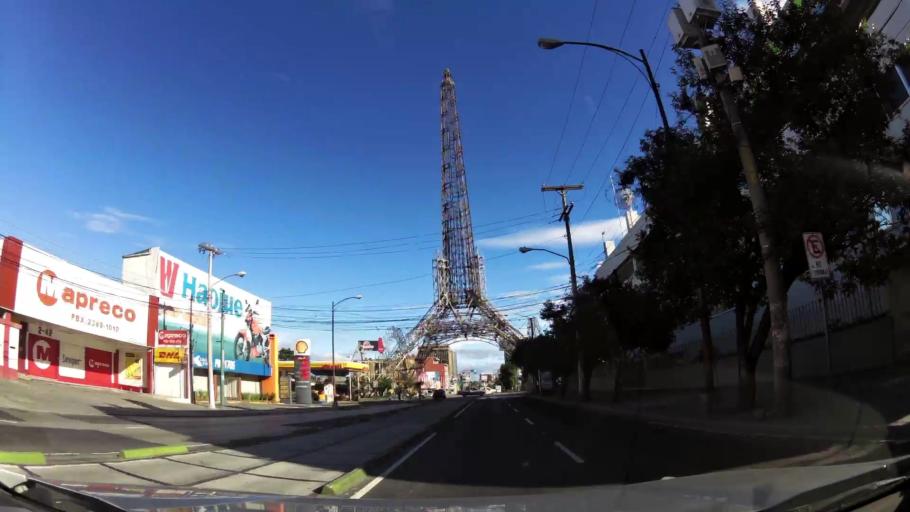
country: GT
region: Guatemala
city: Guatemala City
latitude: 14.6123
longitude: -90.5167
